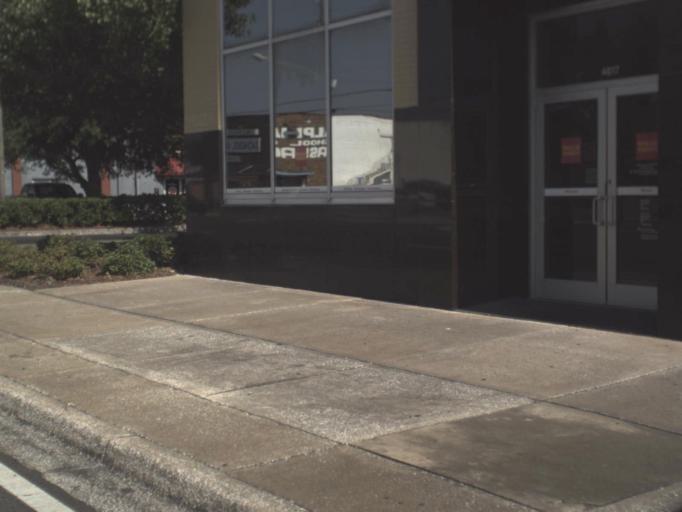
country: US
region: Florida
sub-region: Duval County
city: Jacksonville
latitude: 30.2822
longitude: -81.7248
